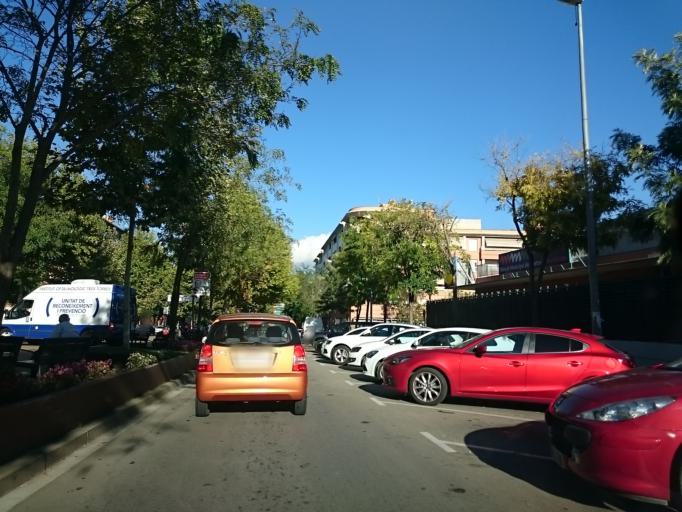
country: ES
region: Catalonia
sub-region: Provincia de Barcelona
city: Martorell
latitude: 41.4768
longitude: 1.9149
